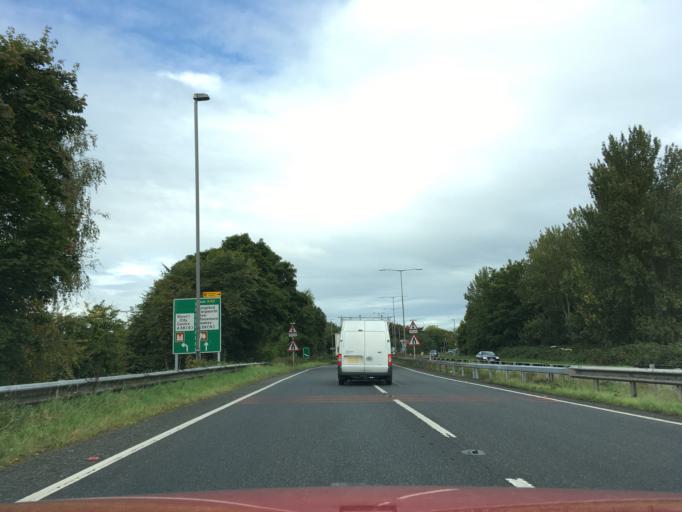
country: GB
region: England
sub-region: Gloucestershire
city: Gloucester
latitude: 51.8819
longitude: -2.2357
